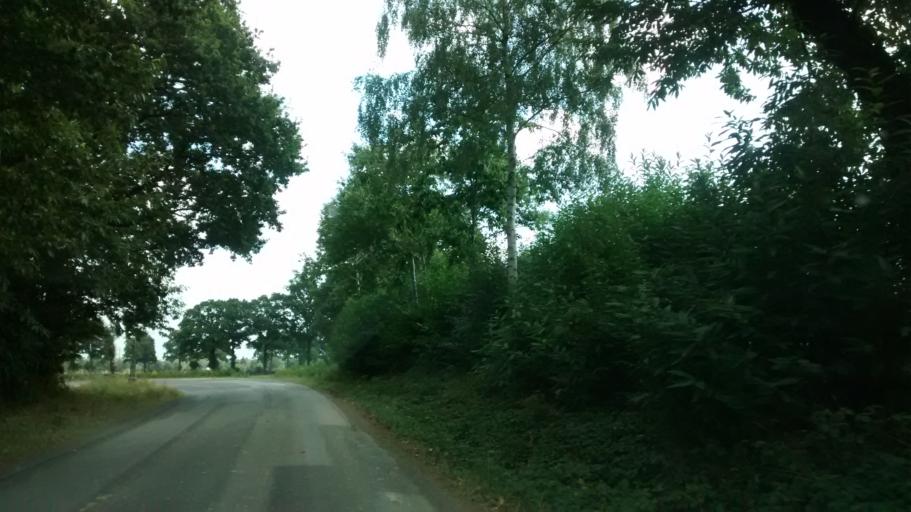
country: FR
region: Brittany
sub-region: Departement d'Ille-et-Vilaine
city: Erbree
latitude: 48.1215
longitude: -1.1113
